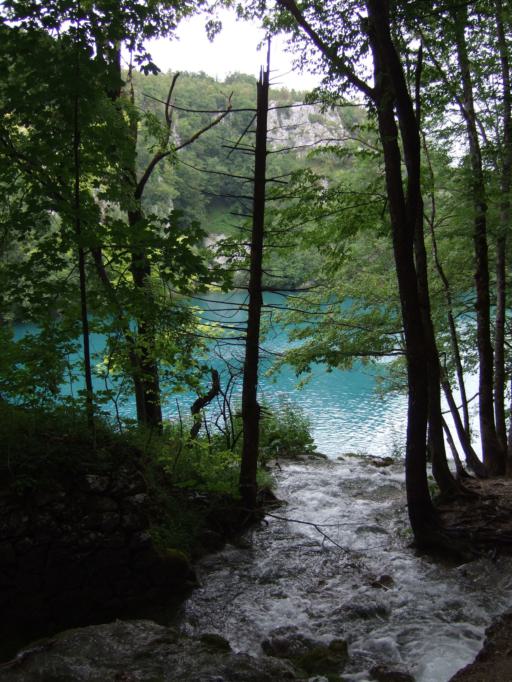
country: HR
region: Licko-Senjska
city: Jezerce
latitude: 44.8945
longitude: 15.6095
